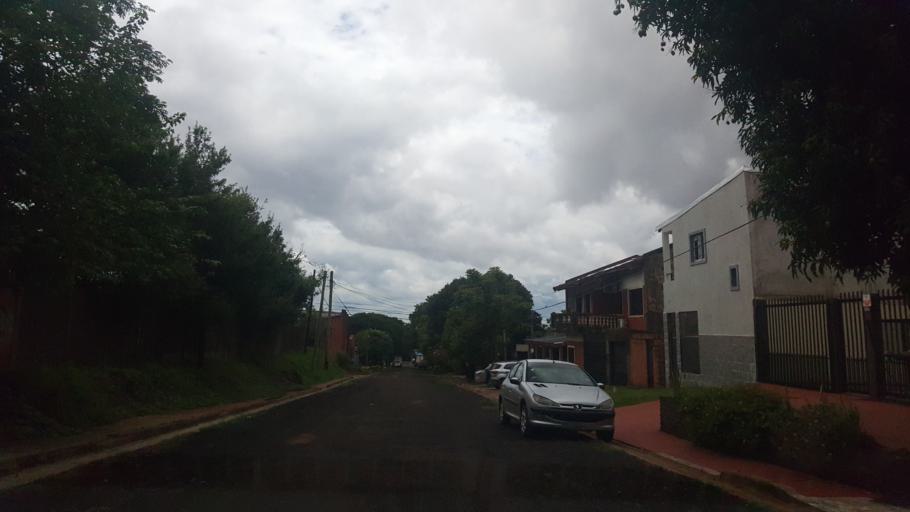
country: AR
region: Misiones
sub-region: Departamento de Capital
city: Posadas
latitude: -27.3909
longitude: -55.9109
